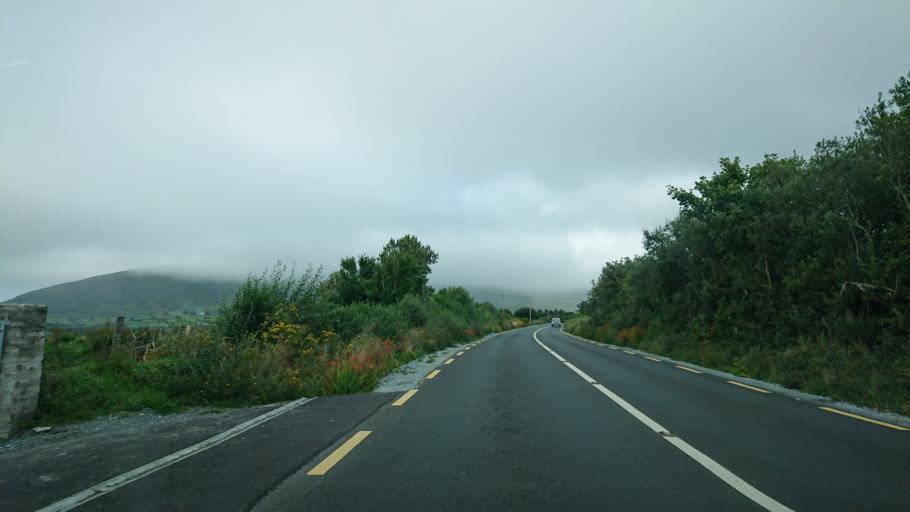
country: IE
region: Munster
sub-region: Ciarrai
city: Cahersiveen
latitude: 51.9538
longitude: -10.1962
